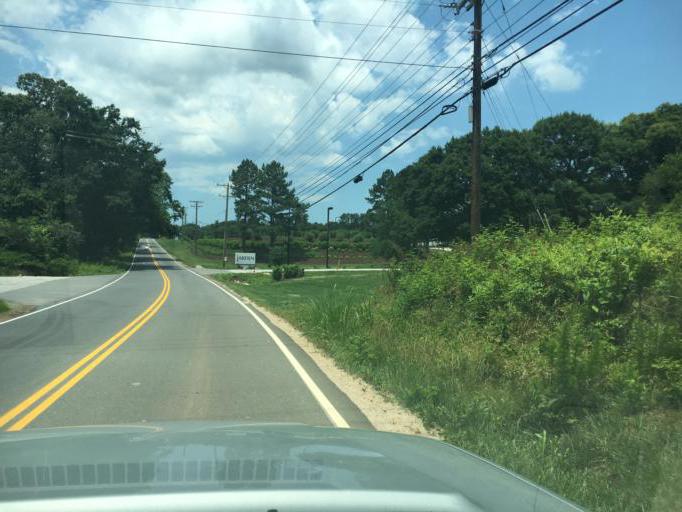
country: US
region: South Carolina
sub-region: Greenville County
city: Five Forks
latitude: 34.8627
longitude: -82.2382
